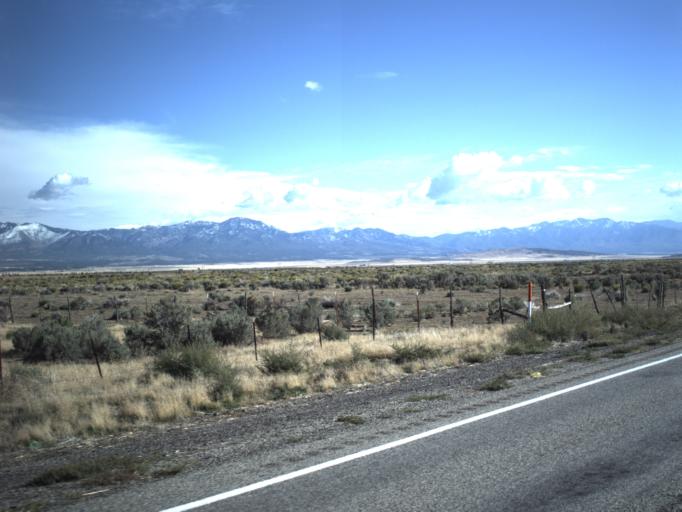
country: US
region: Utah
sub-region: Millard County
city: Fillmore
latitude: 39.1701
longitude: -112.4101
